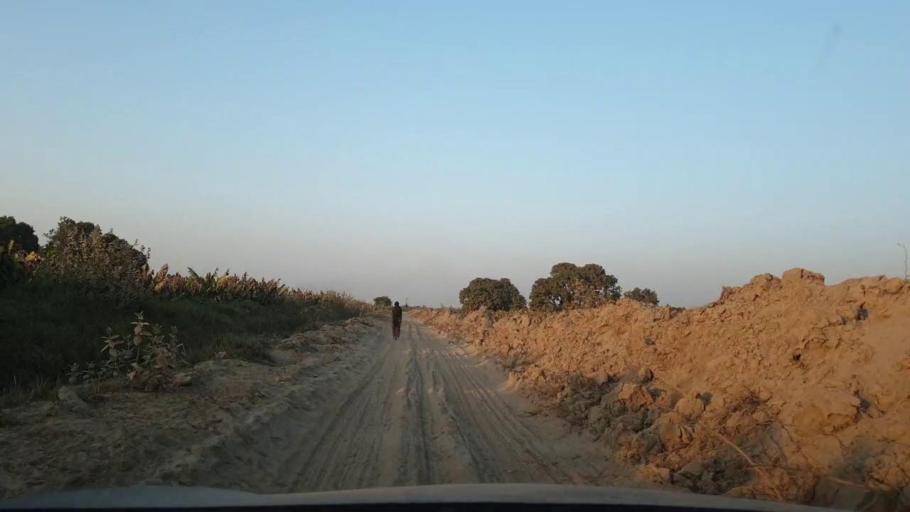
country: PK
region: Sindh
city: Tando Allahyar
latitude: 25.5292
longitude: 68.7361
